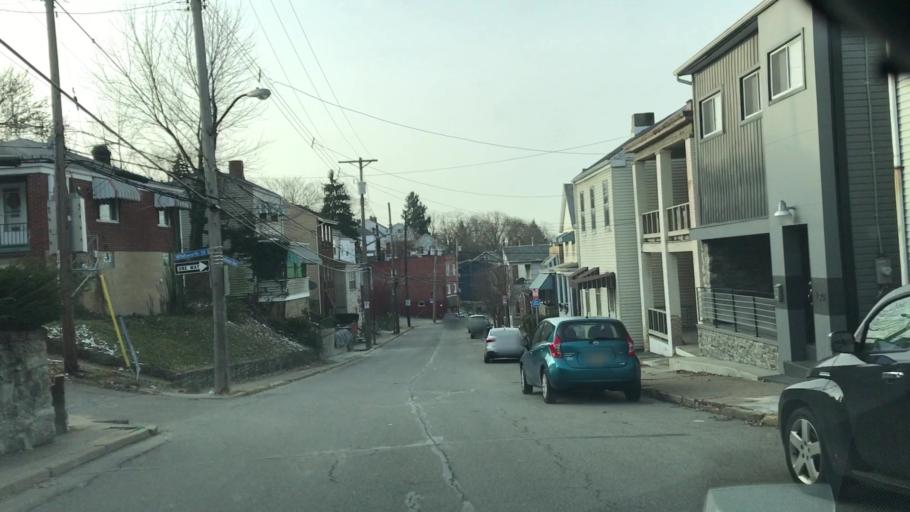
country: US
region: Pennsylvania
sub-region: Allegheny County
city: Pittsburgh
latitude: 40.4261
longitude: -80.0092
